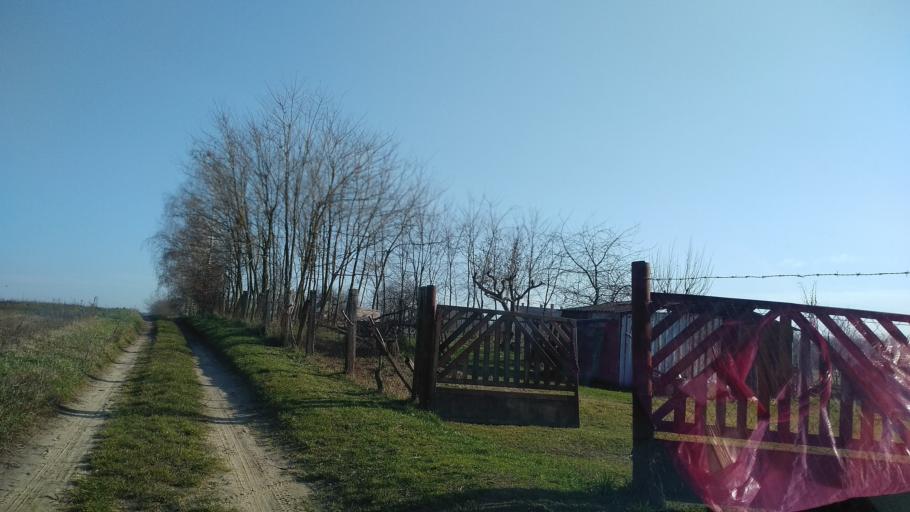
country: HU
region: Somogy
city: Barcs
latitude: 45.9650
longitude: 17.4865
